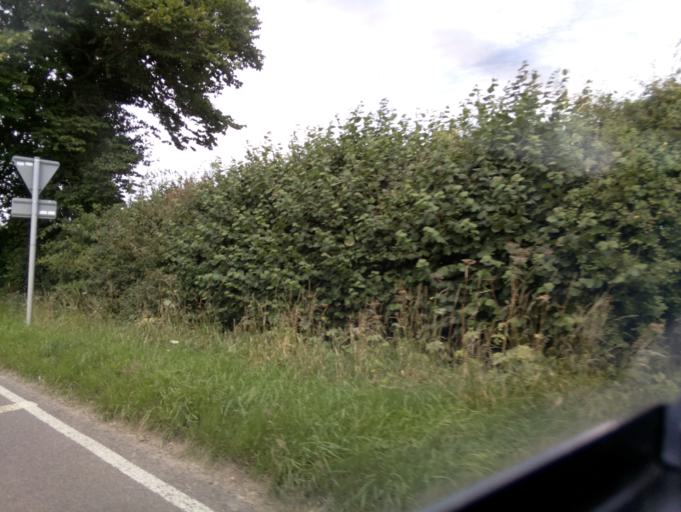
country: GB
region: England
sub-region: Somerset
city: Street
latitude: 51.0832
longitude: -2.6944
